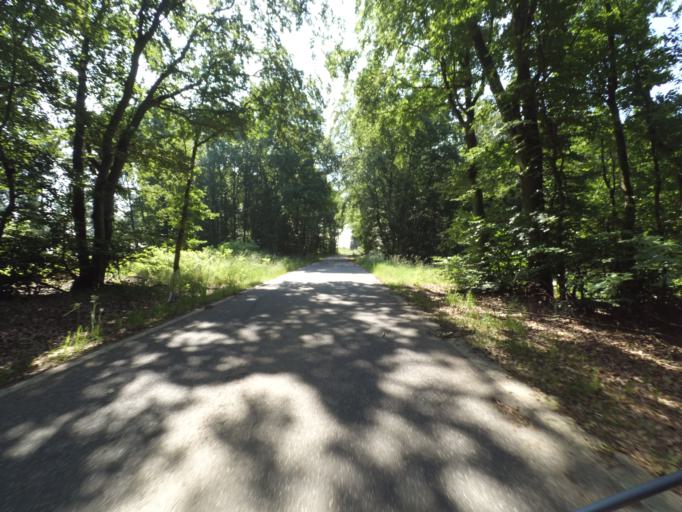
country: DE
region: Rheinland-Pfalz
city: Brodenbach
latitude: 50.2186
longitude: 7.4571
